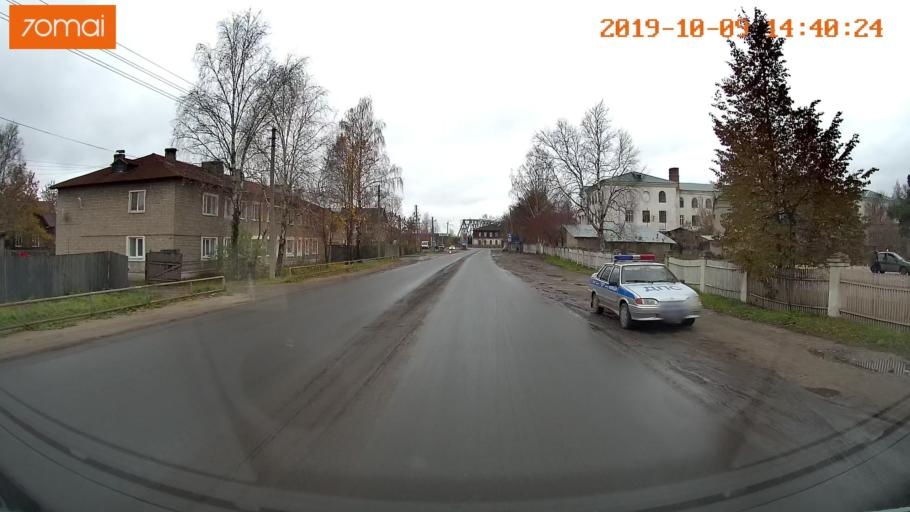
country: RU
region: Kostroma
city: Buy
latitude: 58.4750
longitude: 41.5326
